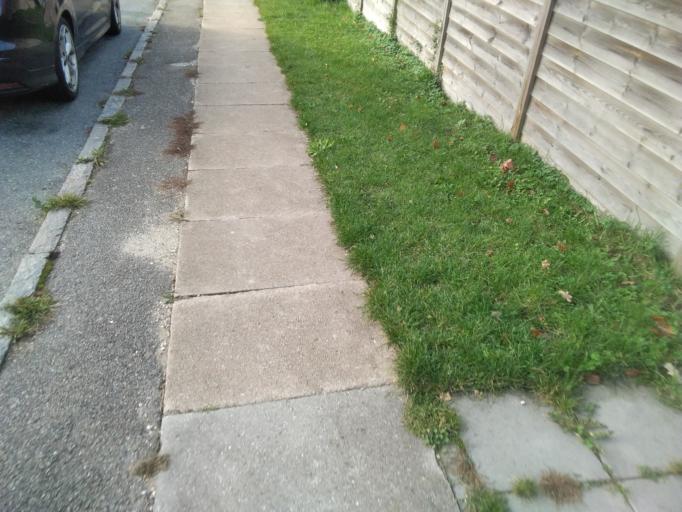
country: DK
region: Capital Region
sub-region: Herlev Kommune
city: Herlev
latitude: 55.7087
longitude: 12.4633
